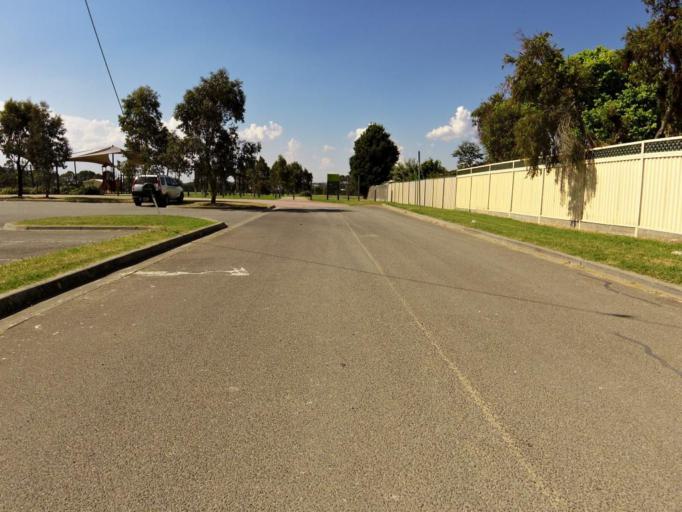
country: AU
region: Victoria
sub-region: Casey
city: Hampton Park
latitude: -38.0228
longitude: 145.2510
